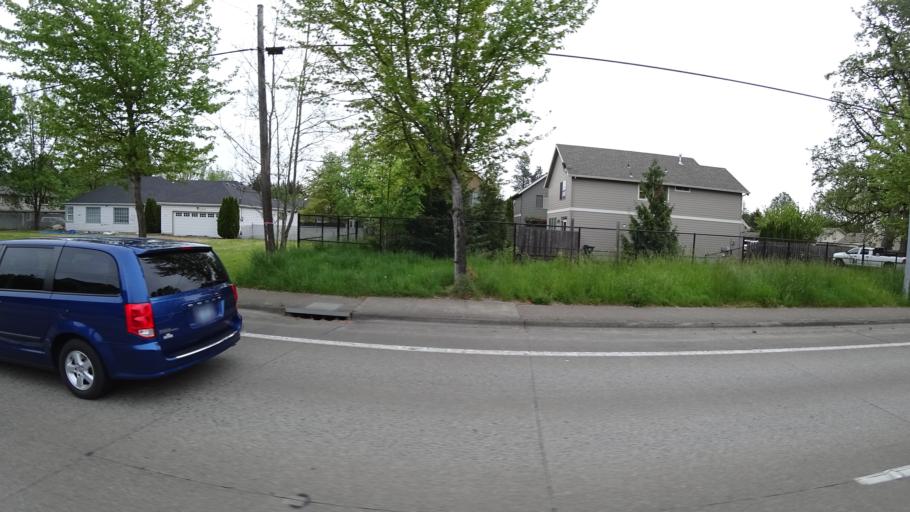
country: US
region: Oregon
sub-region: Washington County
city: Aloha
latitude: 45.5034
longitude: -122.8674
